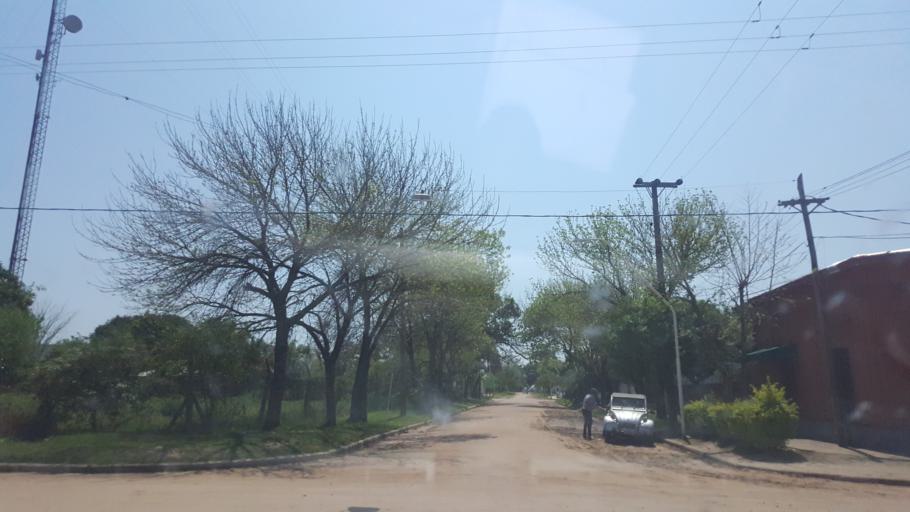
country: AR
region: Corrientes
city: Ita Ibate
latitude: -27.4266
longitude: -57.3367
